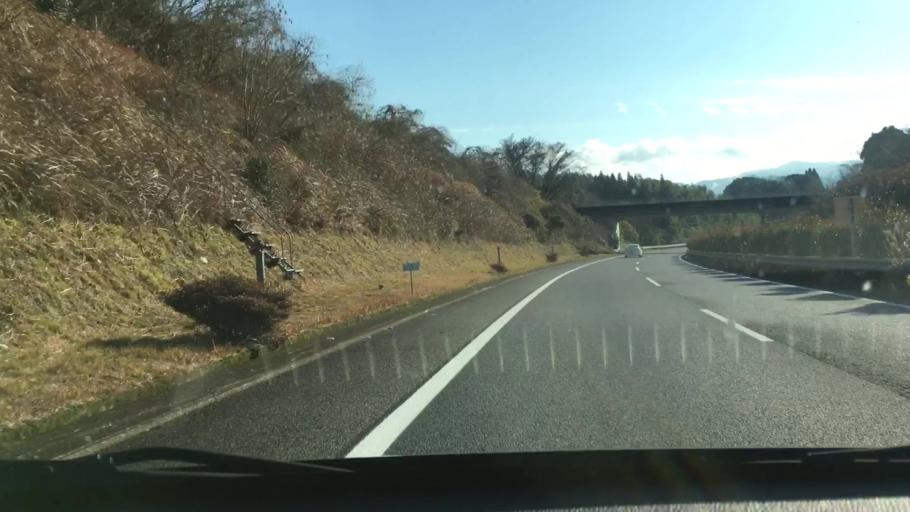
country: JP
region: Kumamoto
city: Hitoyoshi
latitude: 32.2198
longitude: 130.7803
